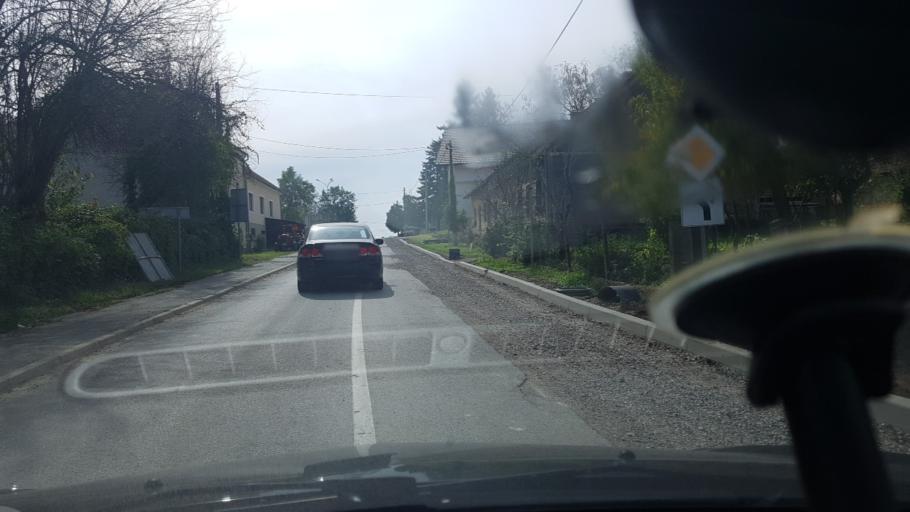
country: HR
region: Varazdinska
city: Remetinec
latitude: 46.1083
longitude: 16.2173
